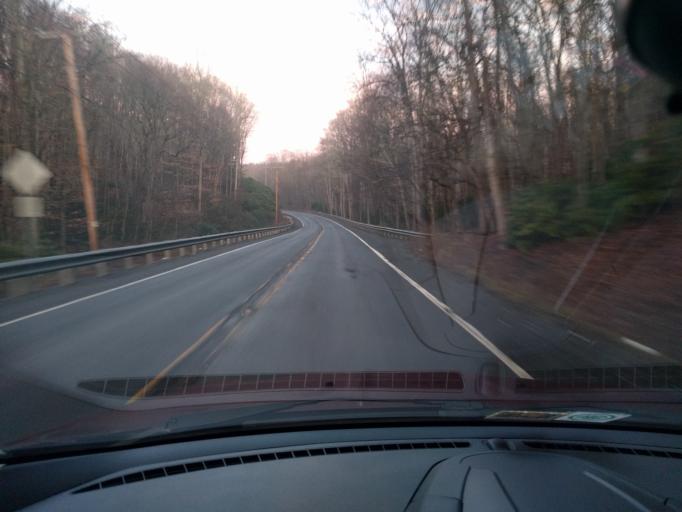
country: US
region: West Virginia
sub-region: Fayette County
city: Fayetteville
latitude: 38.0483
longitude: -80.9418
